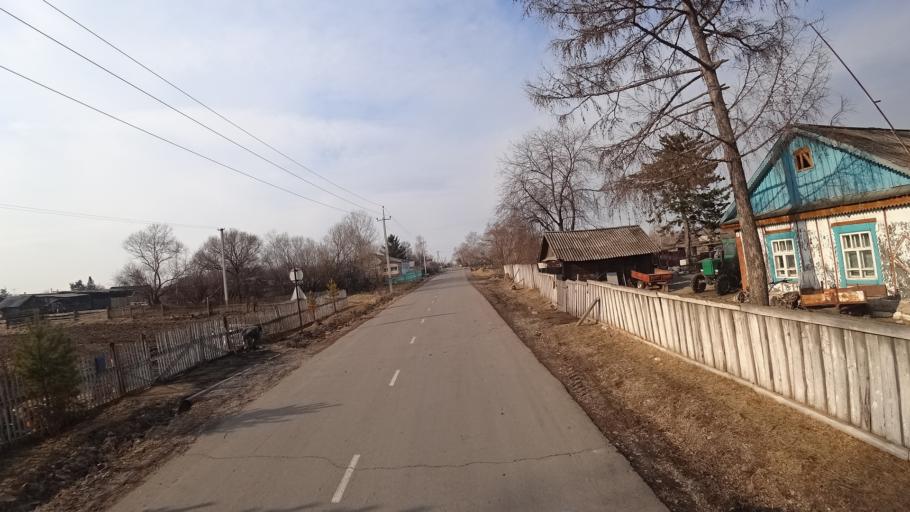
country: RU
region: Amur
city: Novobureyskiy
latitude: 49.8980
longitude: 129.8775
